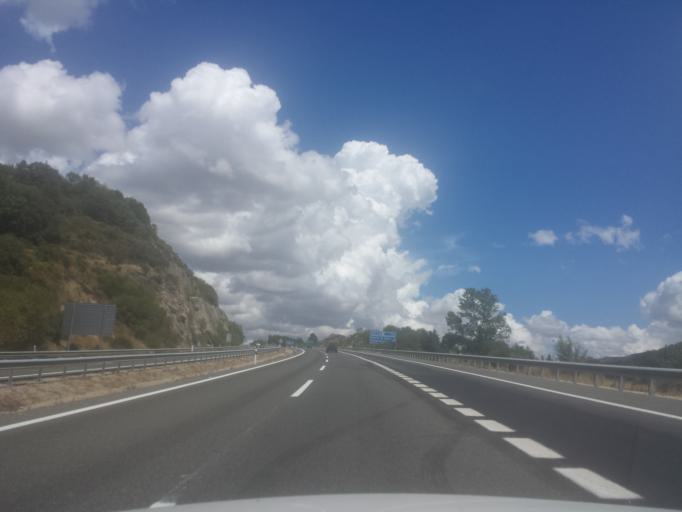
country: ES
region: Castille and Leon
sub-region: Provincia de Salamanca
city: Penacaballera
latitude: 40.3344
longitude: -5.8525
